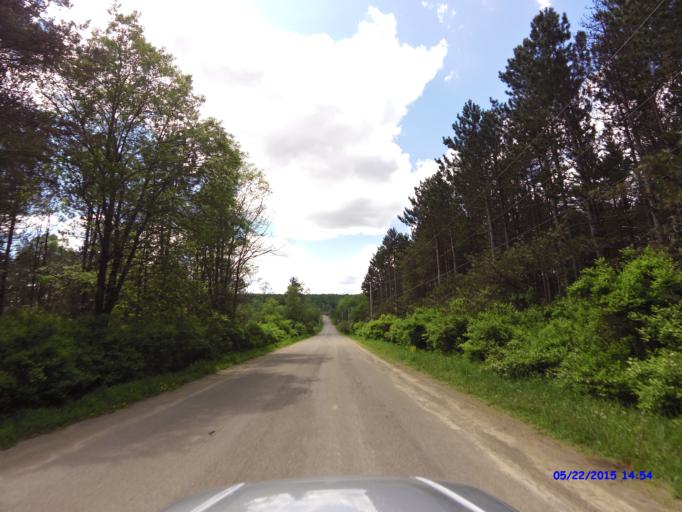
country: US
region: New York
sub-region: Cattaraugus County
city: Franklinville
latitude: 42.3778
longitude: -78.5947
